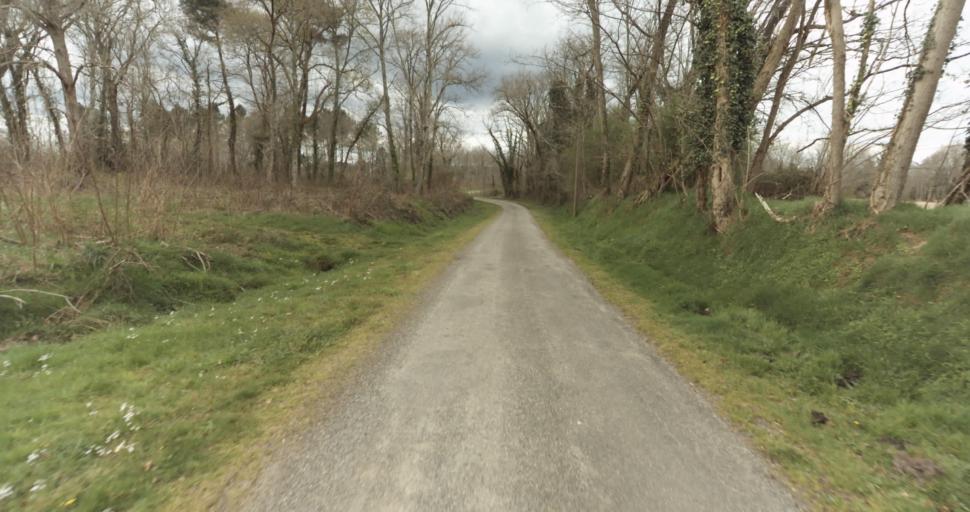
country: FR
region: Aquitaine
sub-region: Departement des Landes
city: Sarbazan
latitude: 44.0145
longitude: -0.3155
